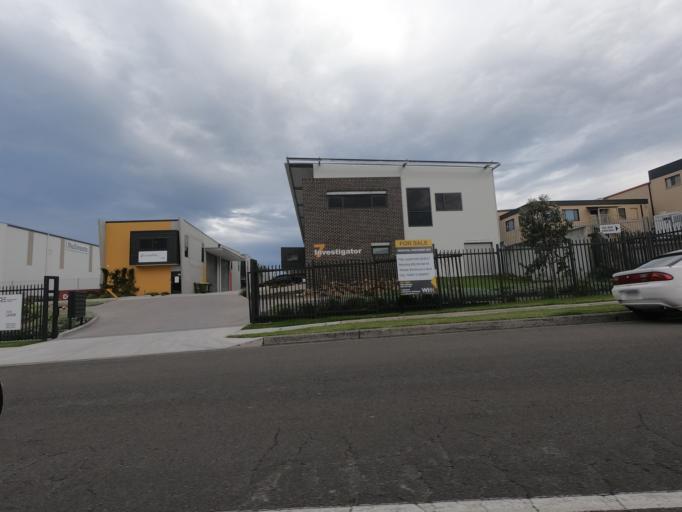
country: AU
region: New South Wales
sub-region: Wollongong
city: Cordeaux Heights
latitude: -34.4581
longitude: 150.8470
